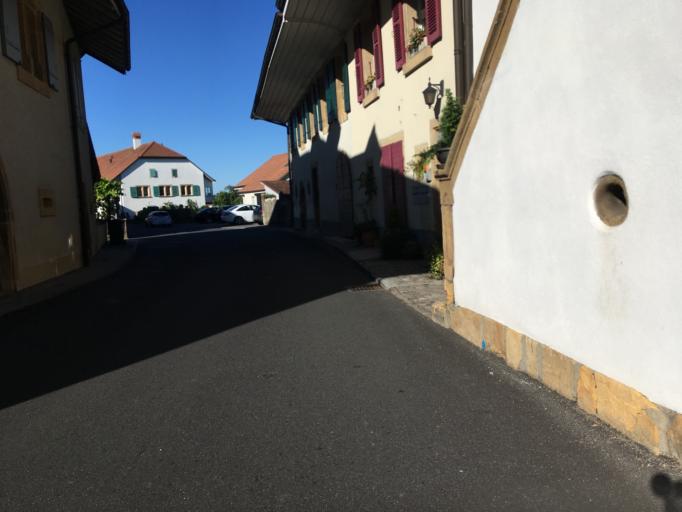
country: CH
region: Fribourg
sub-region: See District
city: Bas-Vully
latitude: 46.9526
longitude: 7.0975
